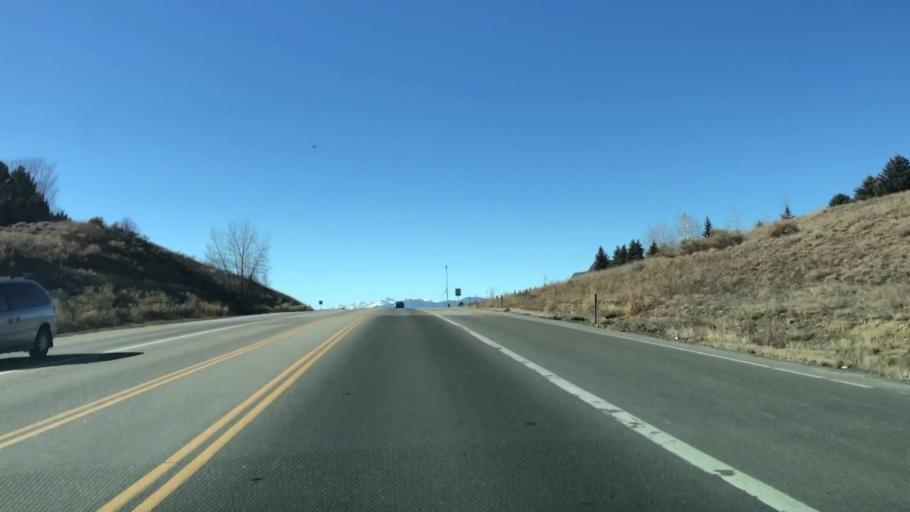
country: US
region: Colorado
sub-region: Weld County
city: Windsor
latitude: 40.4795
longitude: -104.9637
